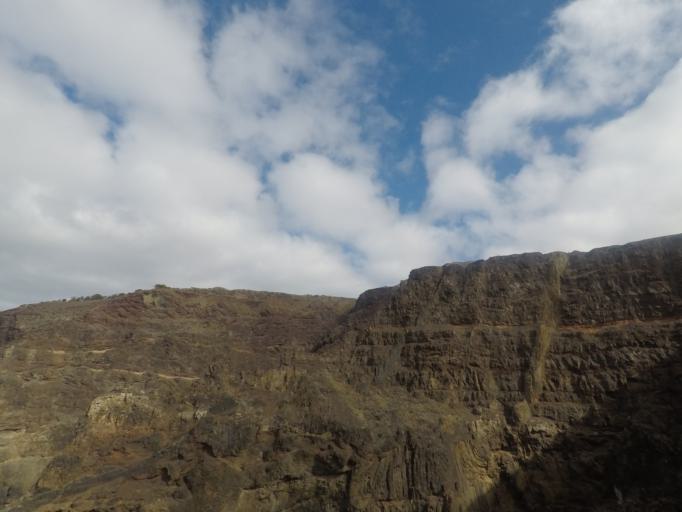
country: PT
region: Madeira
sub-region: Porto Santo
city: Vila de Porto Santo
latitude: 33.0318
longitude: -16.3873
